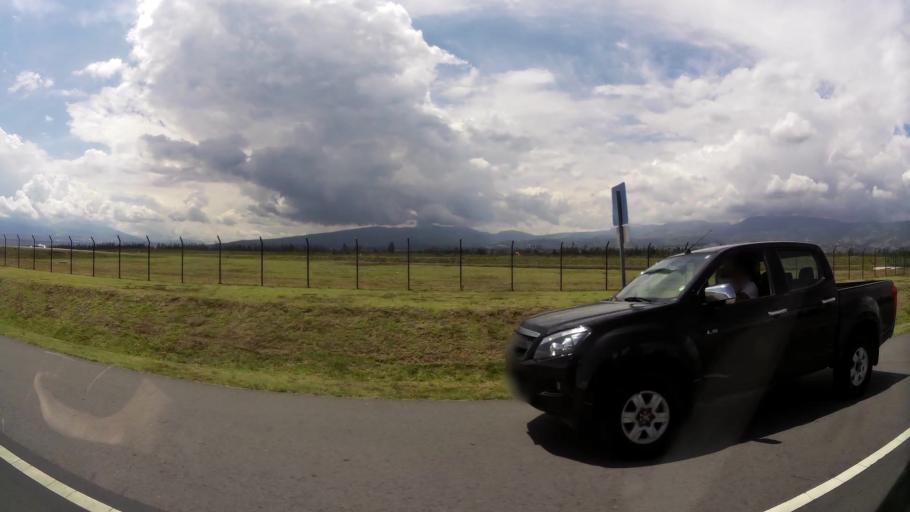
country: EC
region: Pichincha
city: Quito
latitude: -0.1417
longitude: -78.3566
